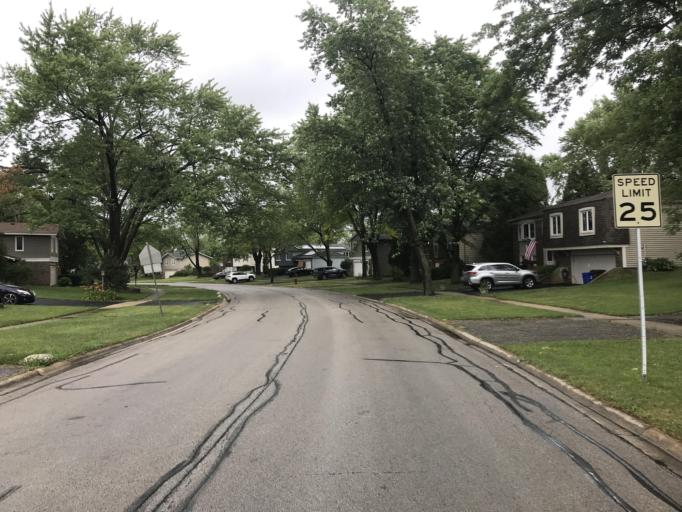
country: US
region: Illinois
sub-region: DuPage County
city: Woodridge
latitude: 41.7409
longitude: -88.0538
